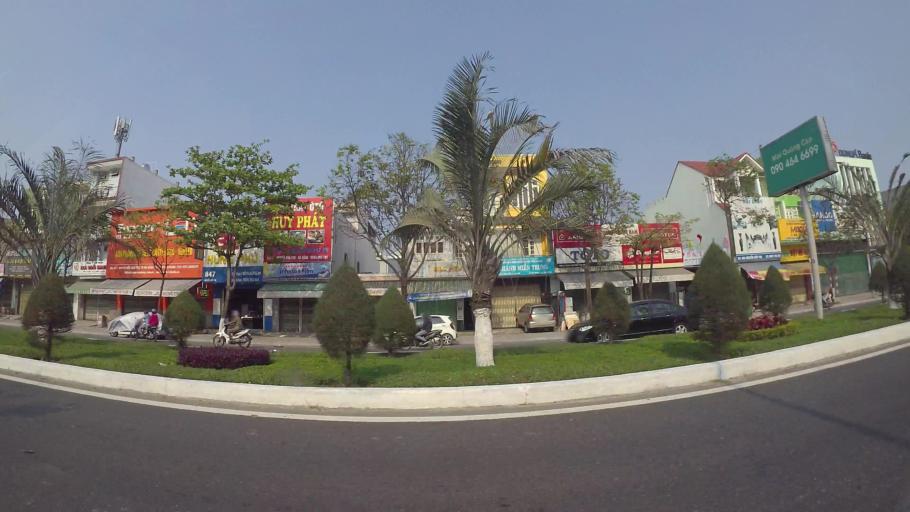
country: VN
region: Da Nang
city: Cam Le
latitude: 16.0224
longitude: 108.2098
